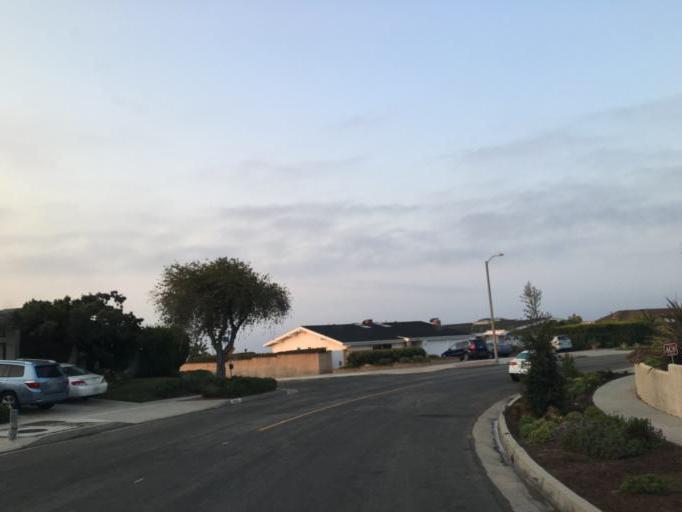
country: US
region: California
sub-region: Los Angeles County
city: Topanga
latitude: 34.0447
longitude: -118.5694
